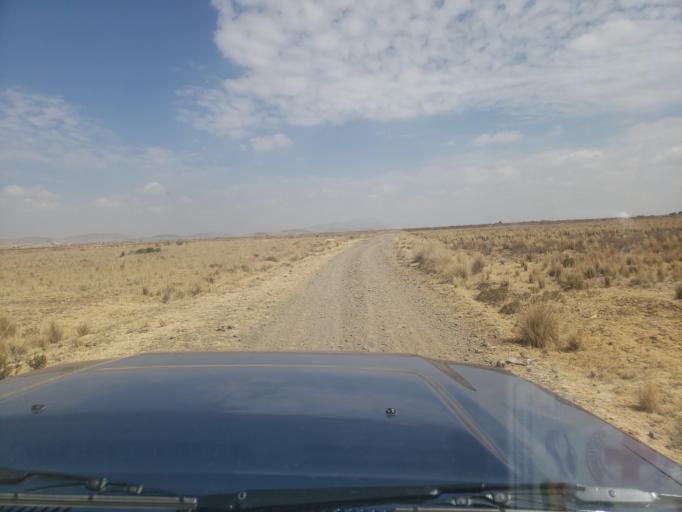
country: BO
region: La Paz
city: Batallas
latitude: -16.4208
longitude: -68.4121
